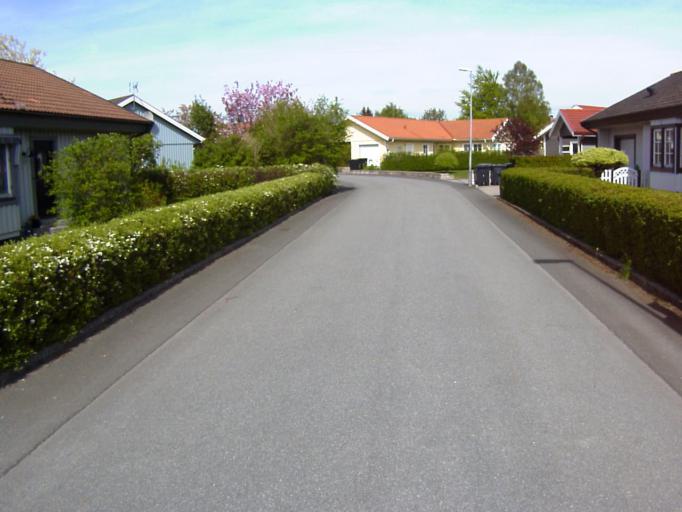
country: SE
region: Skane
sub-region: Kristianstads Kommun
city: Fjalkinge
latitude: 56.1010
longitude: 14.2514
